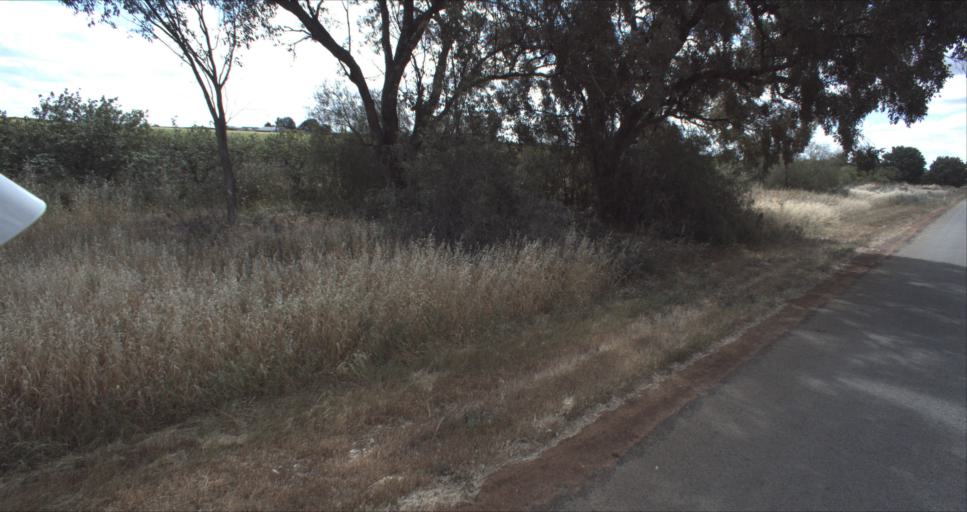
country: AU
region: New South Wales
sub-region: Leeton
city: Leeton
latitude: -34.5870
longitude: 146.3959
